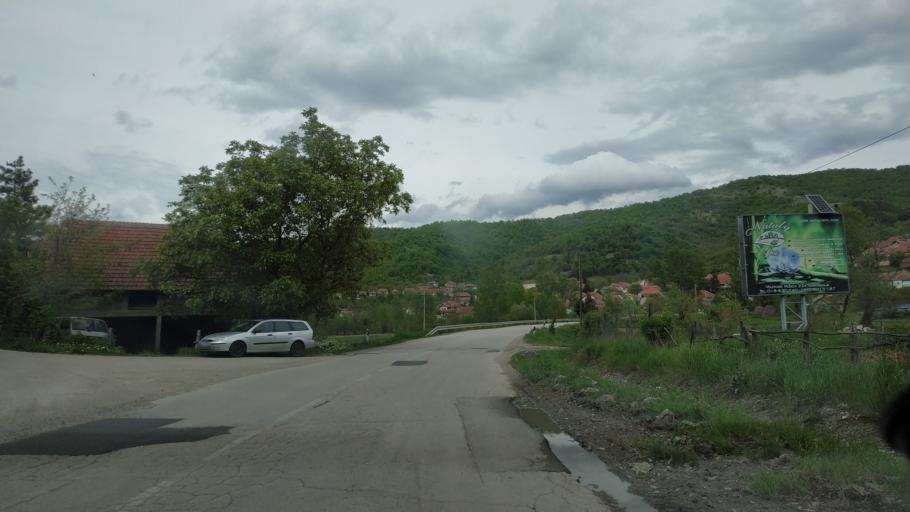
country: RS
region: Central Serbia
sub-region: Nisavski Okrug
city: Aleksinac
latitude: 43.6312
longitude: 21.7154
